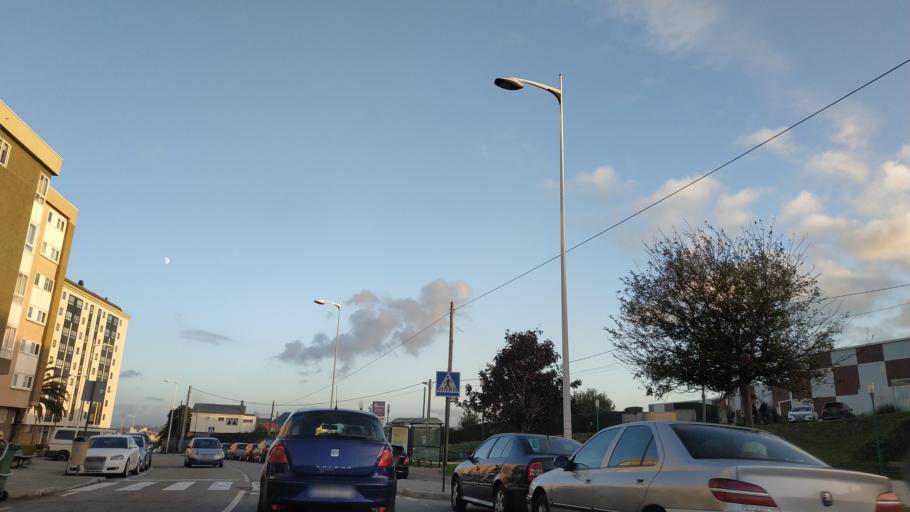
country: ES
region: Galicia
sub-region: Provincia da Coruna
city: A Coruna
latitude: 43.3593
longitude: -8.4264
